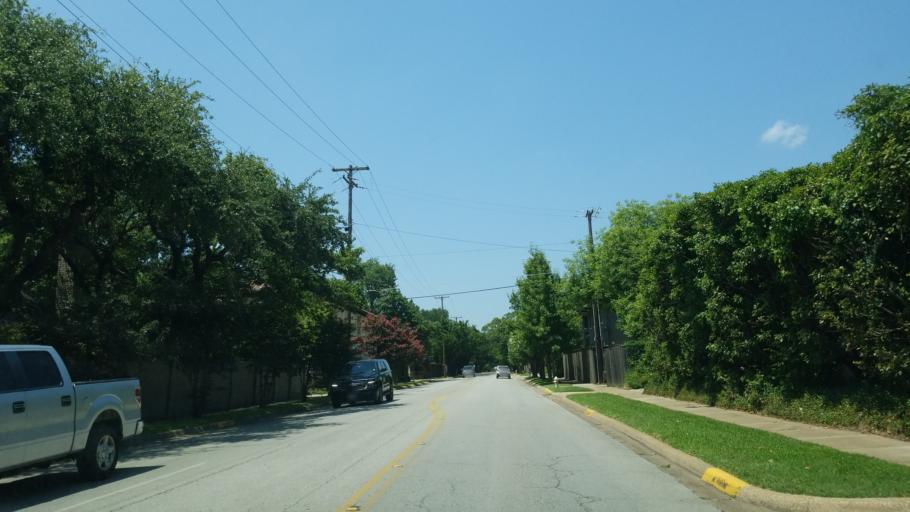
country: US
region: Texas
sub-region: Dallas County
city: Highland Park
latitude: 32.8302
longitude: -96.7871
